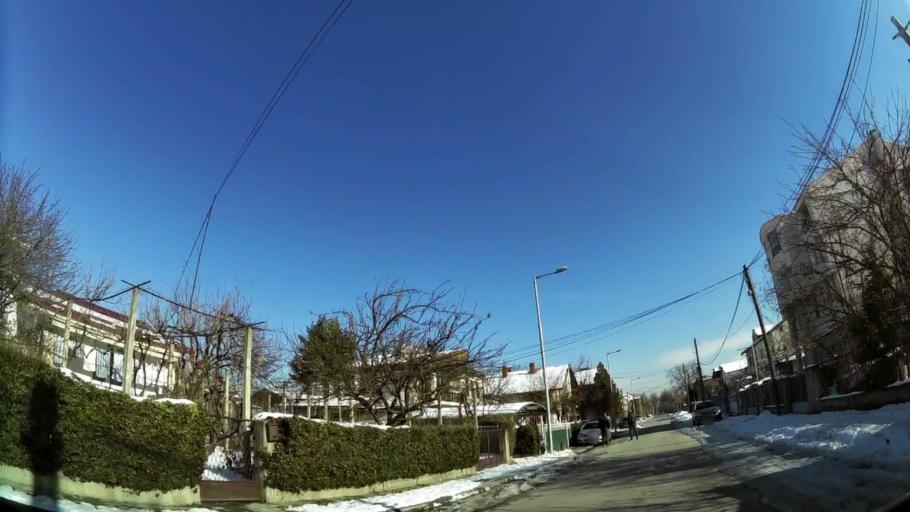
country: MK
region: Saraj
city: Saraj
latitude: 42.0045
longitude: 21.3491
